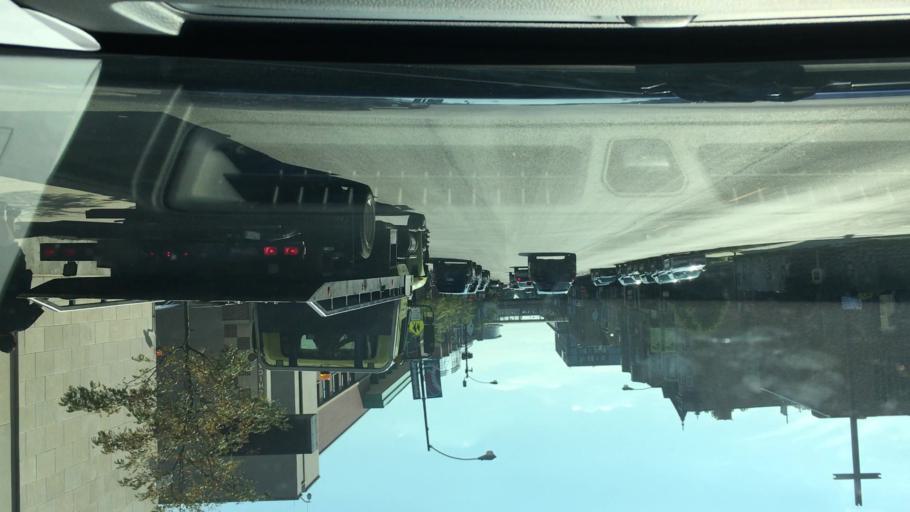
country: US
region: Illinois
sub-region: Cook County
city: Chicago
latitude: 41.9473
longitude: -87.6503
